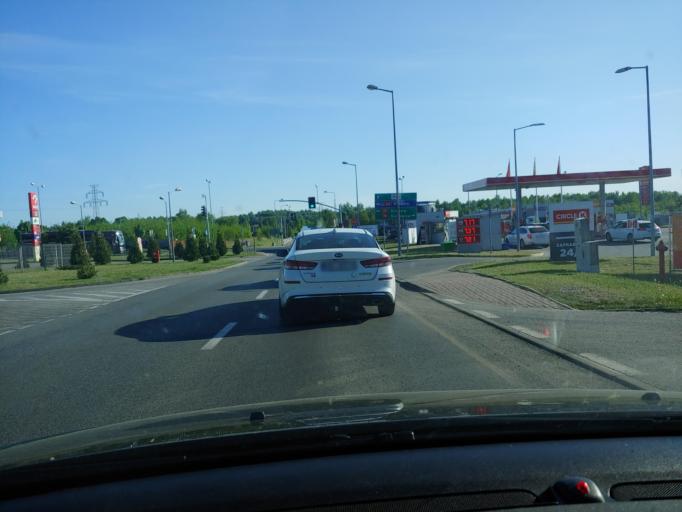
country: PL
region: Silesian Voivodeship
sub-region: Jaworzno
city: Jaworzno
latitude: 50.1861
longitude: 19.2875
